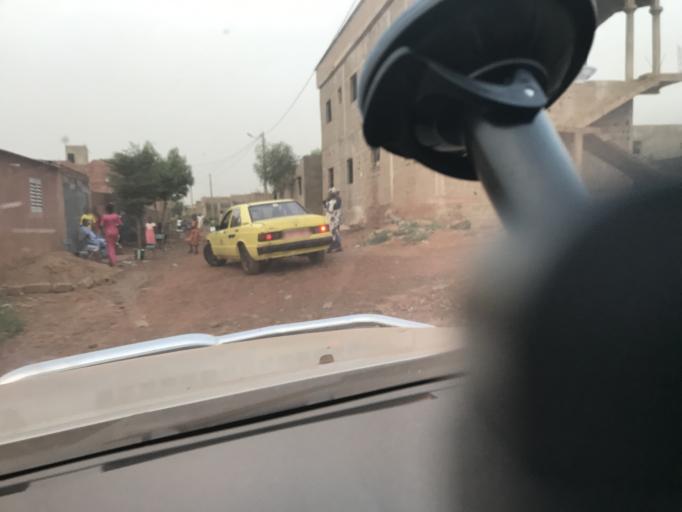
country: ML
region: Bamako
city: Bamako
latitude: 12.6490
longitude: -7.8813
